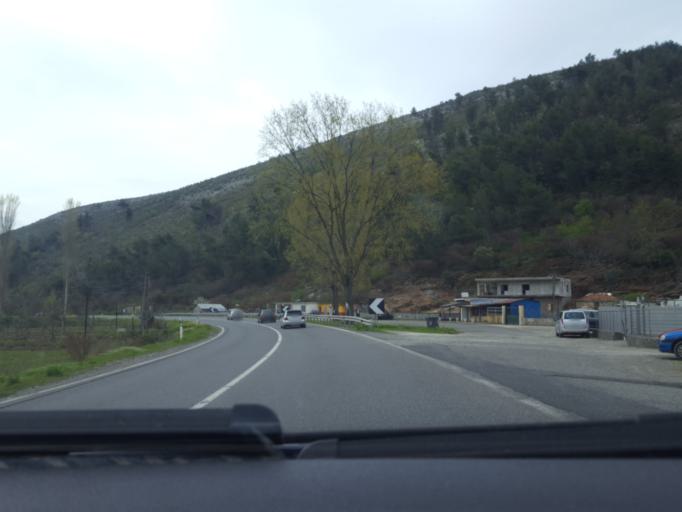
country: AL
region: Lezhe
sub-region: Rrethi i Lezhes
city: Balldreni i Ri
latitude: 41.8027
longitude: 19.6304
